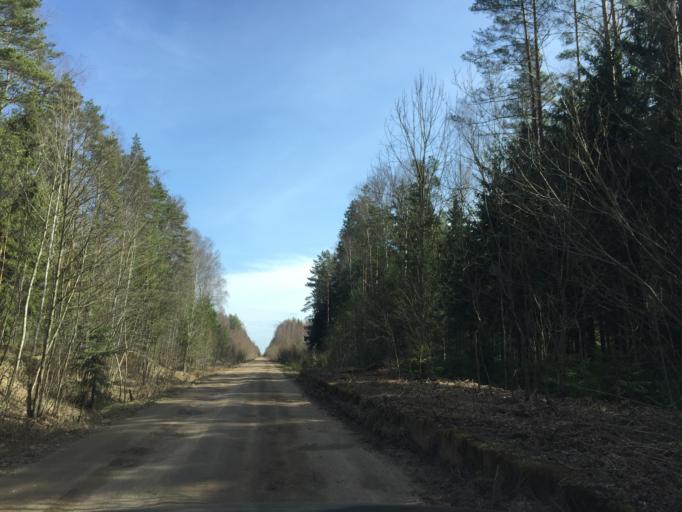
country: LV
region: Salaspils
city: Salaspils
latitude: 56.9223
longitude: 24.4286
